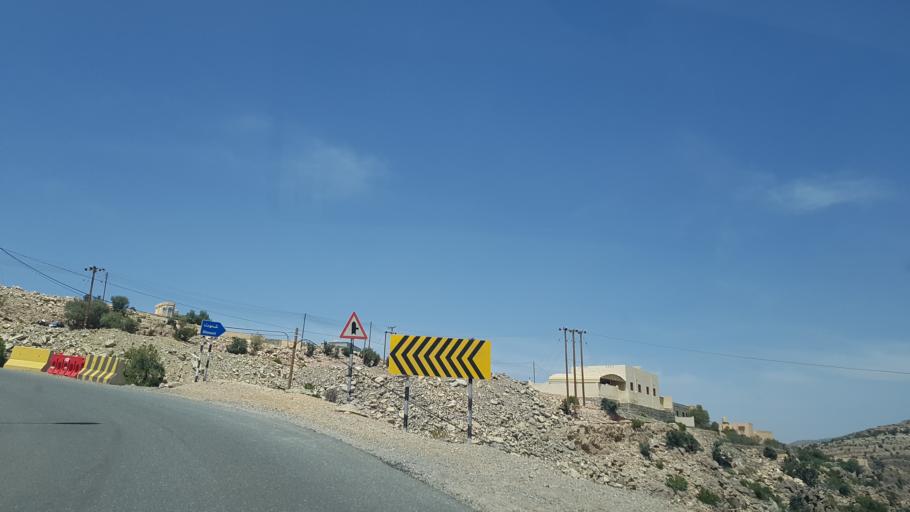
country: OM
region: Muhafazat ad Dakhiliyah
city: Izki
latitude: 23.1139
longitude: 57.6601
